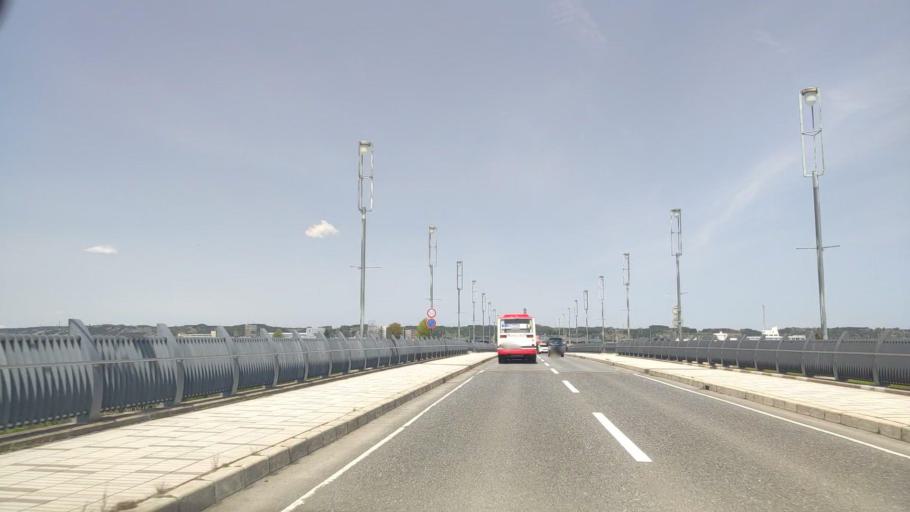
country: JP
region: Aomori
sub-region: Hachinohe Shi
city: Uchimaru
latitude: 40.5009
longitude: 141.4432
